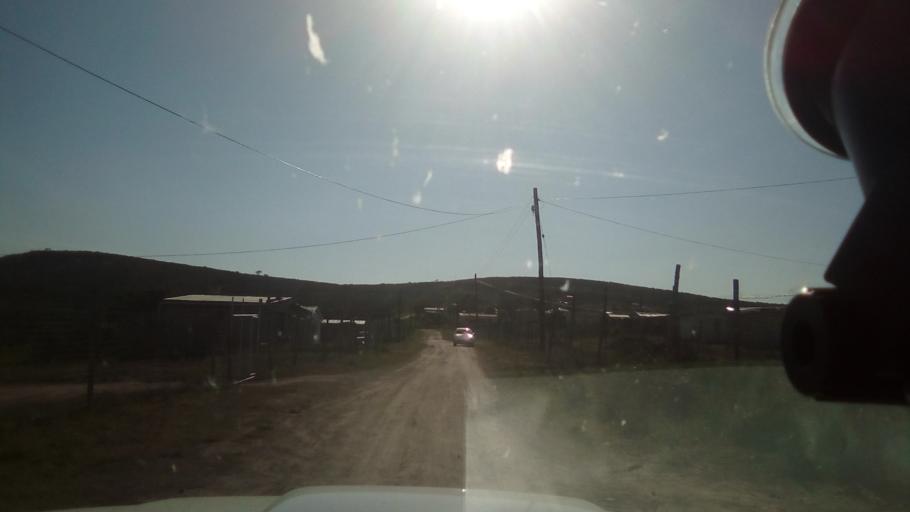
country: ZA
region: Eastern Cape
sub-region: Buffalo City Metropolitan Municipality
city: Bhisho
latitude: -32.8203
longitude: 27.3532
